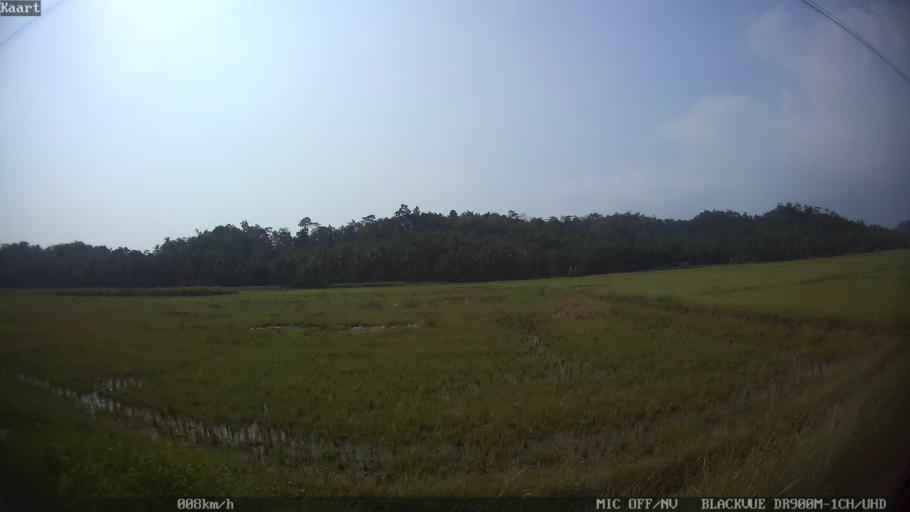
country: ID
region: Lampung
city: Kedondong
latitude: -5.4082
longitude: 105.0173
